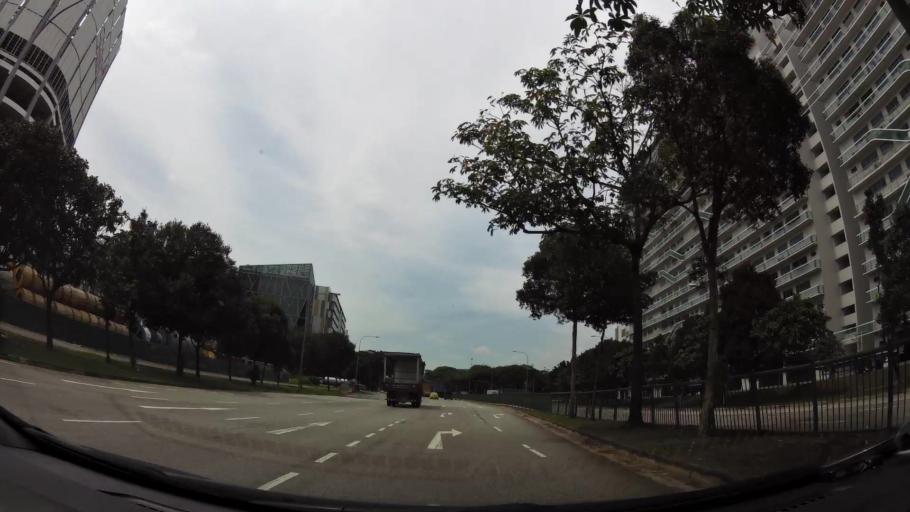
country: SG
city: Singapore
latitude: 1.3149
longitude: 103.6972
